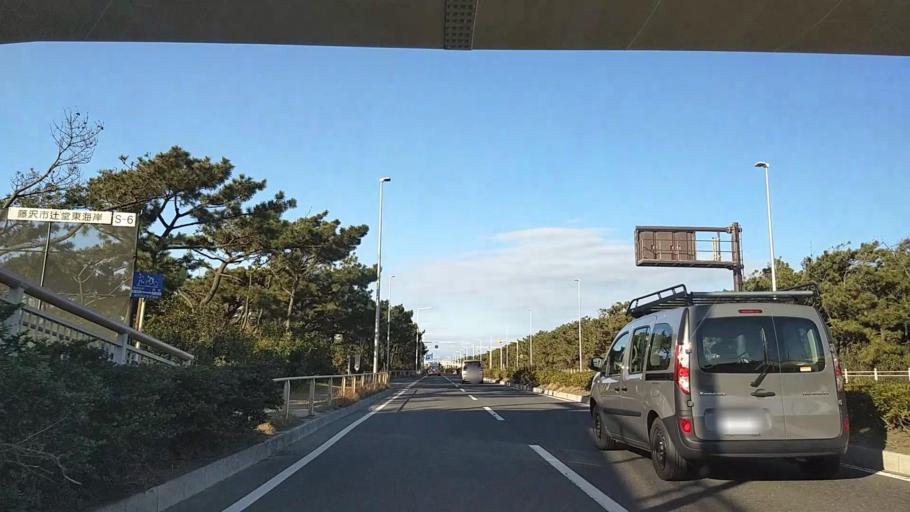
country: JP
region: Kanagawa
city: Fujisawa
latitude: 35.3182
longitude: 139.4582
